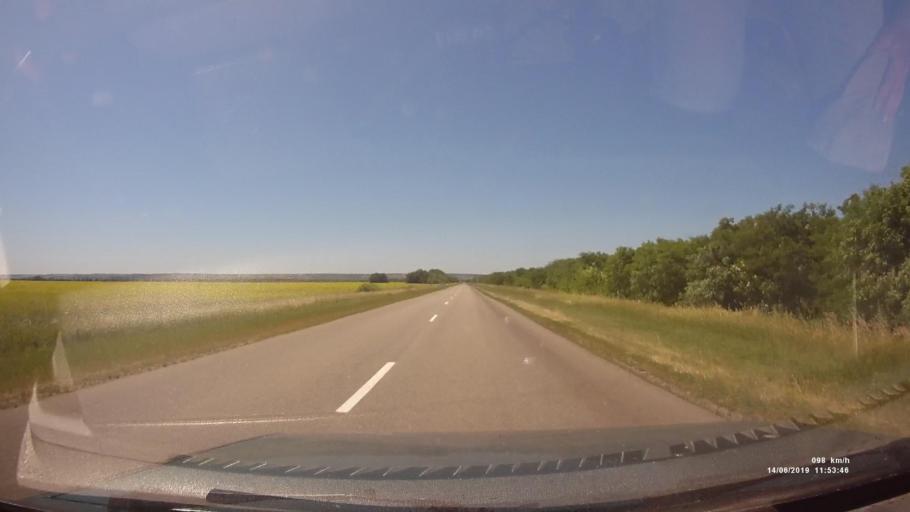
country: RU
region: Rostov
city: Kazanskaya
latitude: 49.8246
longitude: 41.2060
